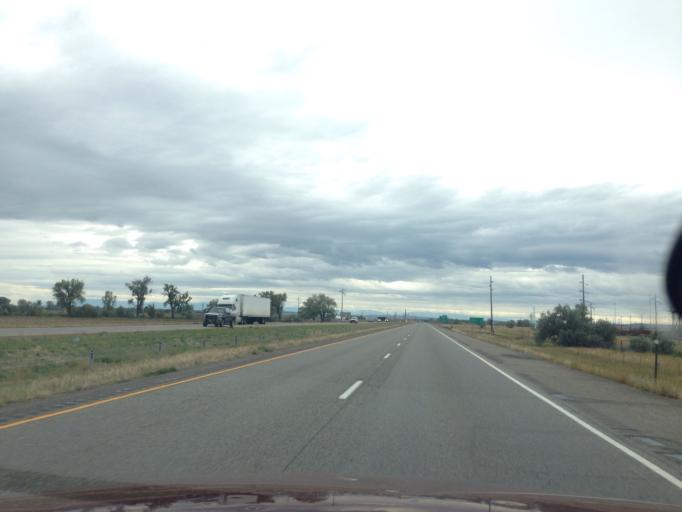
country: US
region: Montana
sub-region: Yellowstone County
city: Laurel
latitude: 45.6779
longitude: -108.7215
